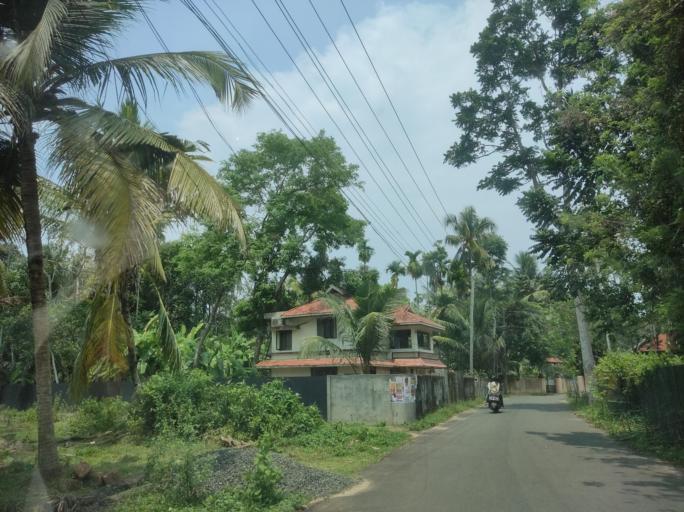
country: IN
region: Kerala
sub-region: Alappuzha
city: Vayalar
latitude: 9.7365
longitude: 76.3277
